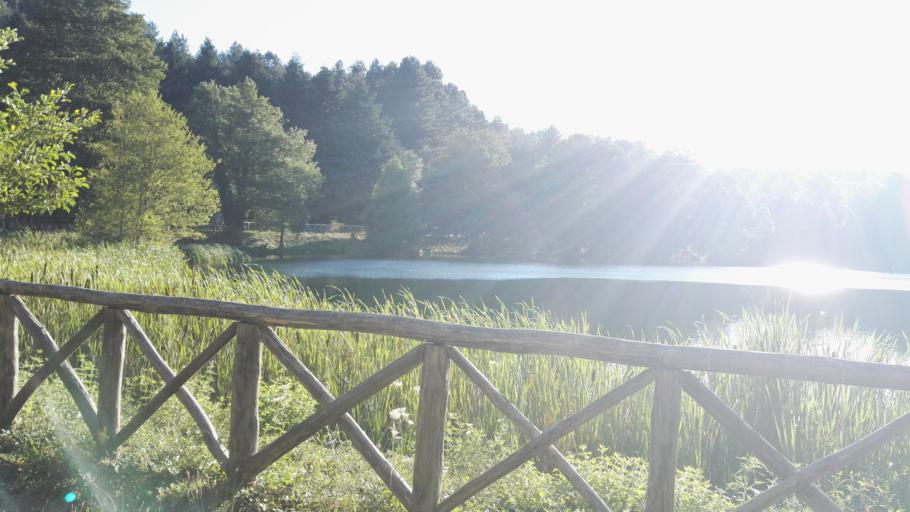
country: IT
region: Calabria
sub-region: Provincia di Vibo-Valentia
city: Mongiana
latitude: 38.5211
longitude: 16.3059
